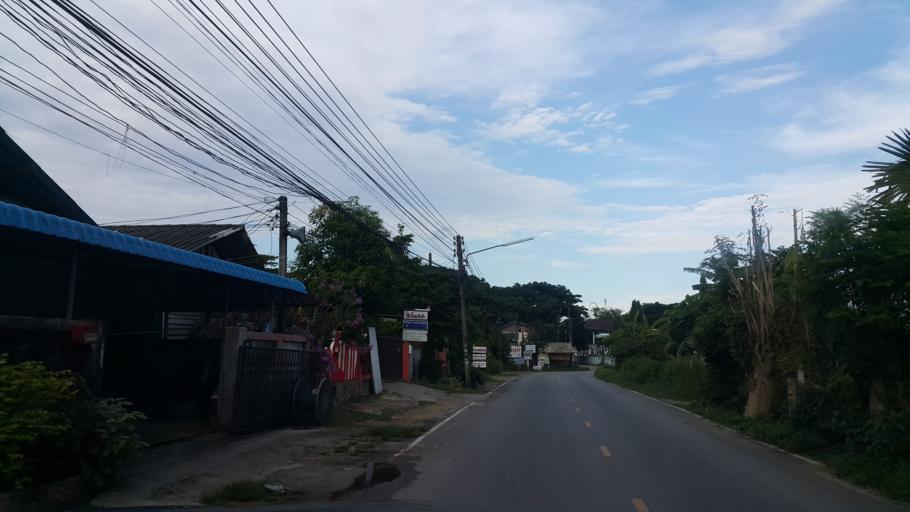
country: TH
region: Chiang Rai
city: Chiang Rai
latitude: 19.9250
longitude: 99.8461
